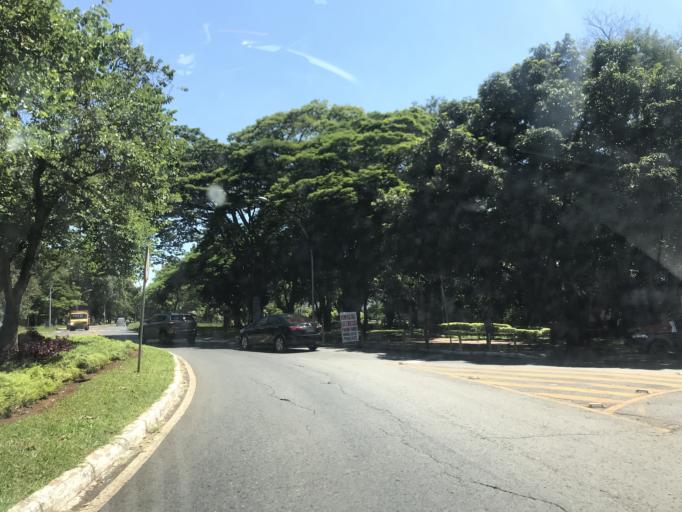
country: BR
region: Federal District
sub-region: Brasilia
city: Brasilia
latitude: -15.8158
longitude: -47.8936
